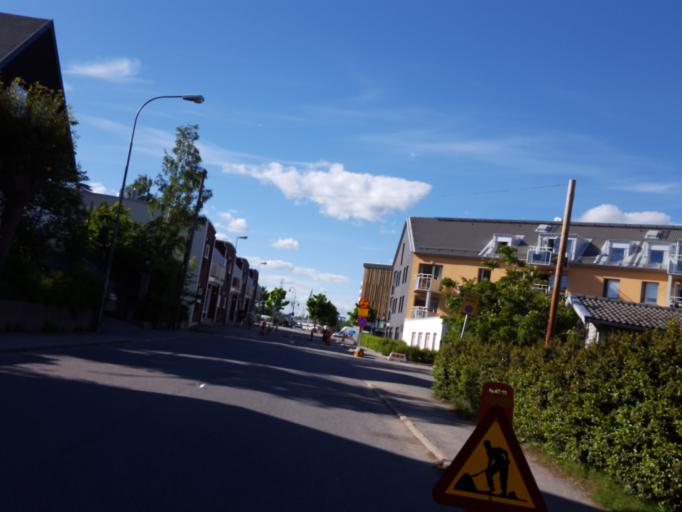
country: SE
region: Stockholm
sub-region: Sollentuna Kommun
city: Sollentuna
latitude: 59.4350
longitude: 17.9381
